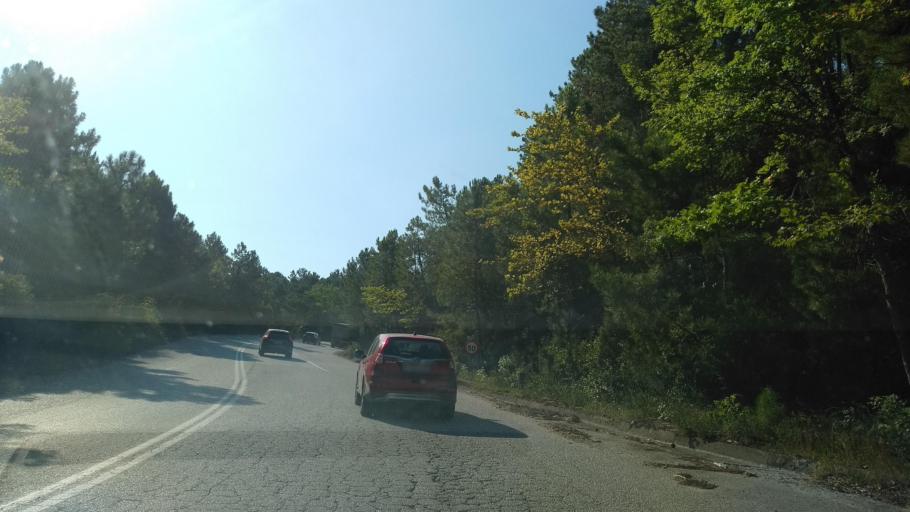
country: GR
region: Central Macedonia
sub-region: Nomos Chalkidikis
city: Stratonion
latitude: 40.5553
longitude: 23.8238
